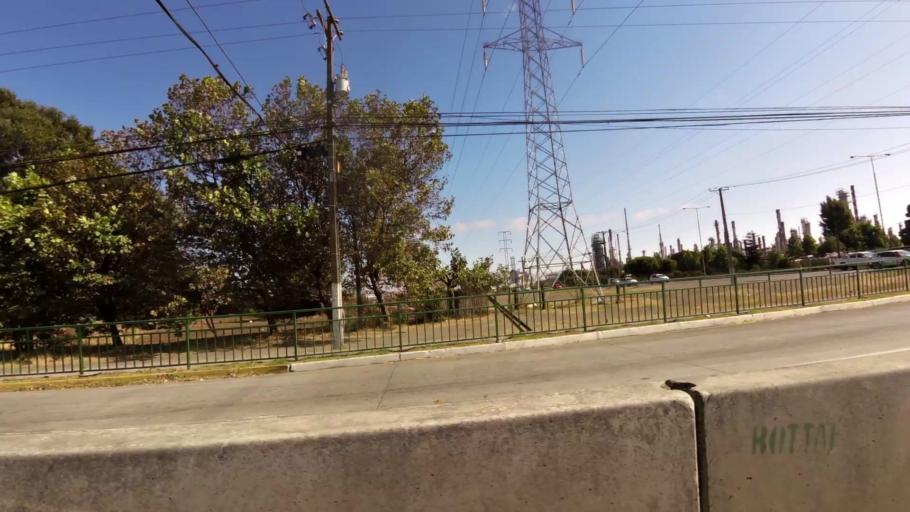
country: CL
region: Biobio
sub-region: Provincia de Concepcion
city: Talcahuano
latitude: -36.7758
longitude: -73.1152
